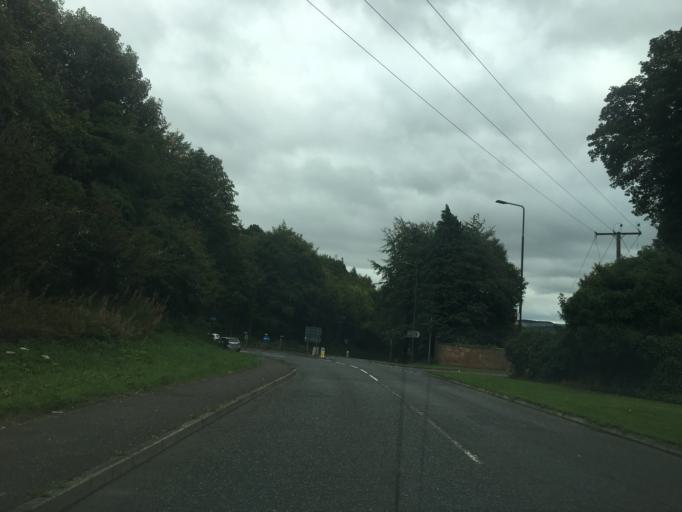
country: GB
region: Scotland
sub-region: Midlothian
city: Dalkeith
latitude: 55.8950
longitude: -3.0927
